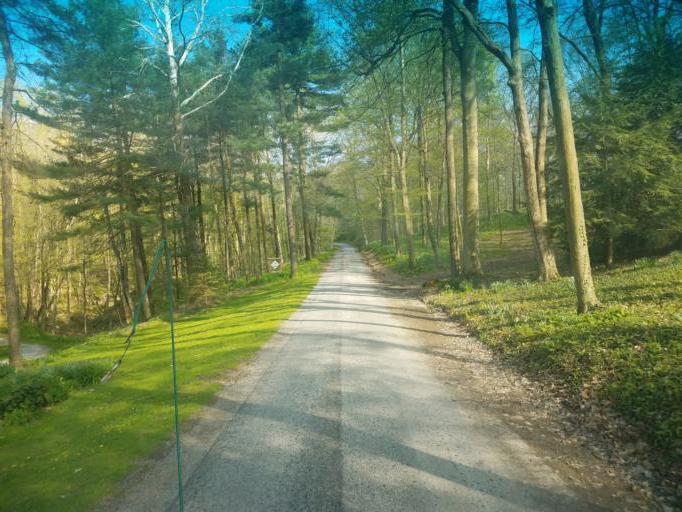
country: US
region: Ohio
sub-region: Wayne County
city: Shreve
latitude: 40.6828
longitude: -81.9376
